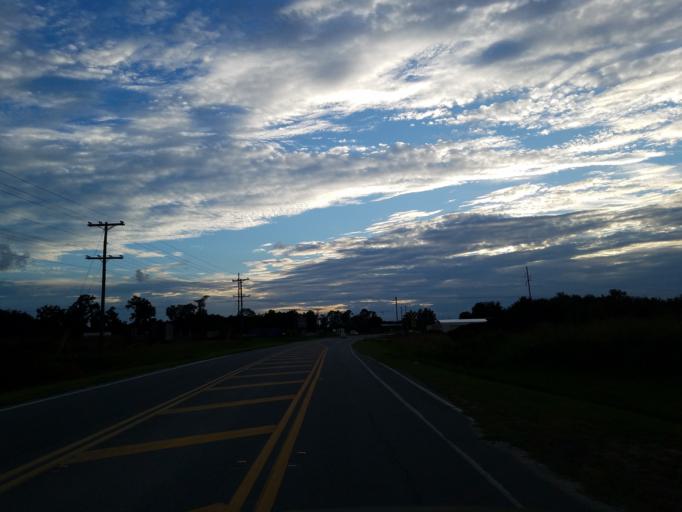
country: US
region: Georgia
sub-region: Cook County
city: Adel
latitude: 31.1459
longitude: -83.4255
